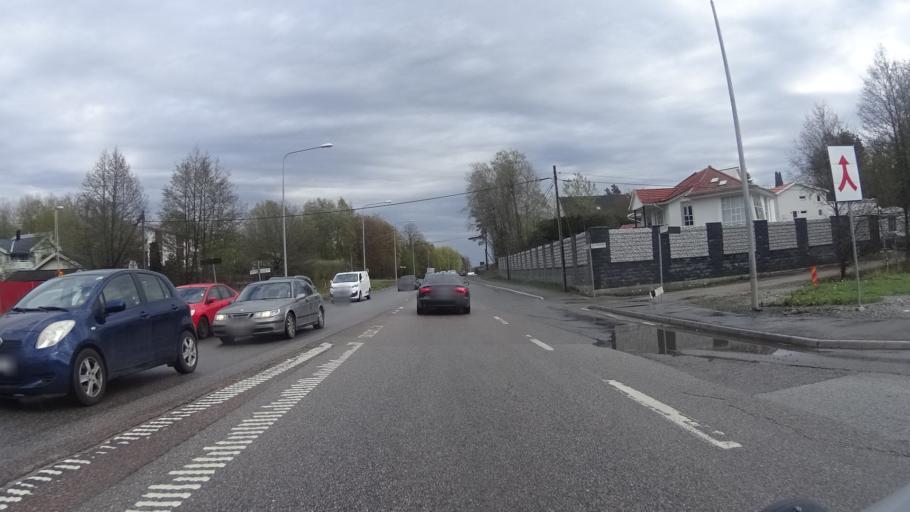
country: SE
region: Stockholm
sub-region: Botkyrka Kommun
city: Tullinge
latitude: 59.2371
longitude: 17.9133
